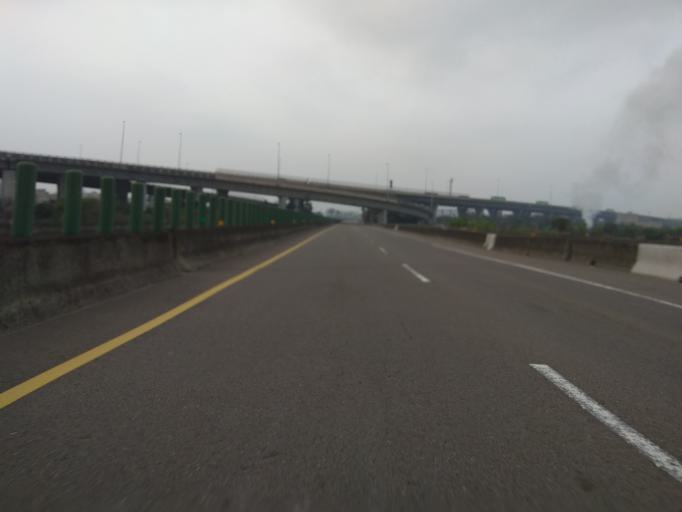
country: TW
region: Taiwan
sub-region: Hsinchu
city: Hsinchu
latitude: 24.7033
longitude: 120.8670
